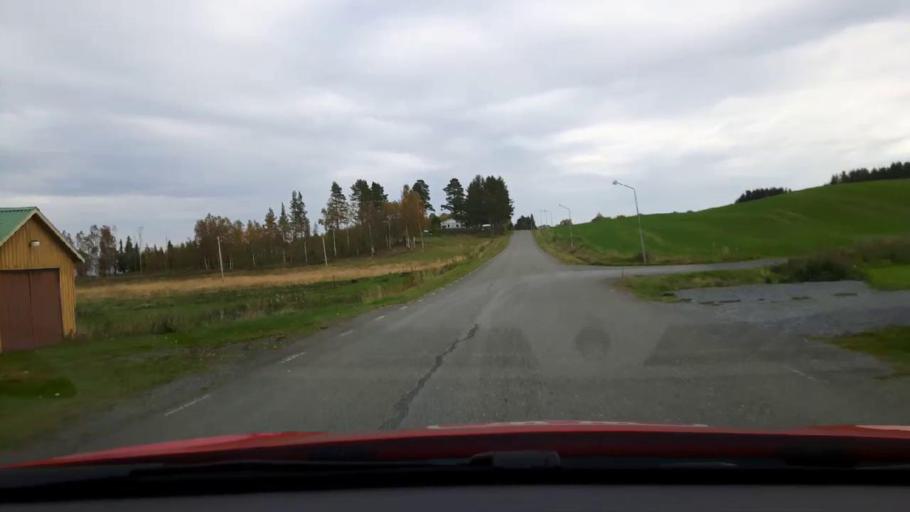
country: SE
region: Jaemtland
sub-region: Krokoms Kommun
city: Krokom
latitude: 63.2302
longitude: 14.1274
